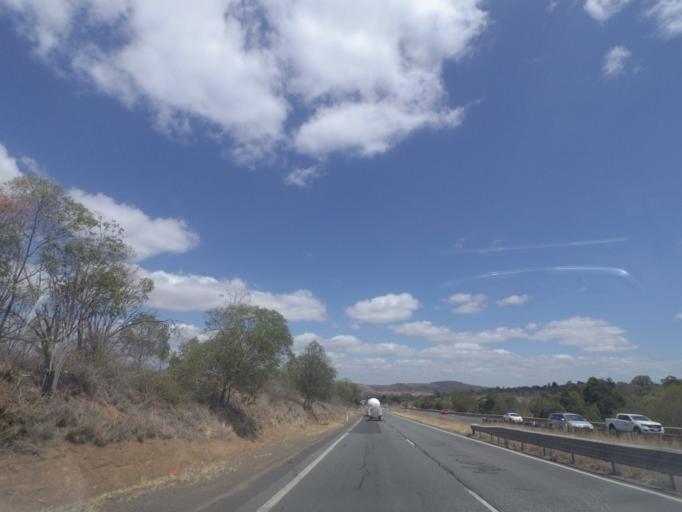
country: AU
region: Queensland
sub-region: Ipswich
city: Thagoona
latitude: -27.5627
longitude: 152.5545
